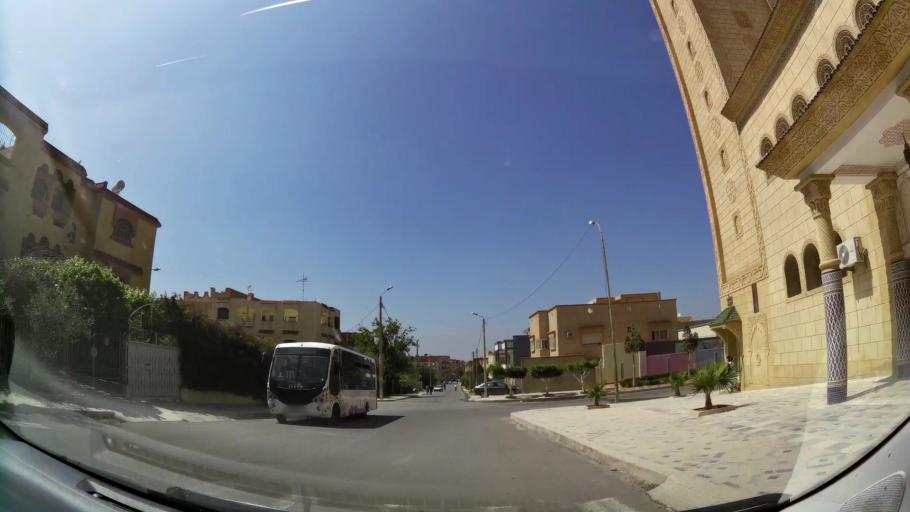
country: MA
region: Oriental
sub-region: Oujda-Angad
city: Oujda
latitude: 34.6920
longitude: -1.8811
